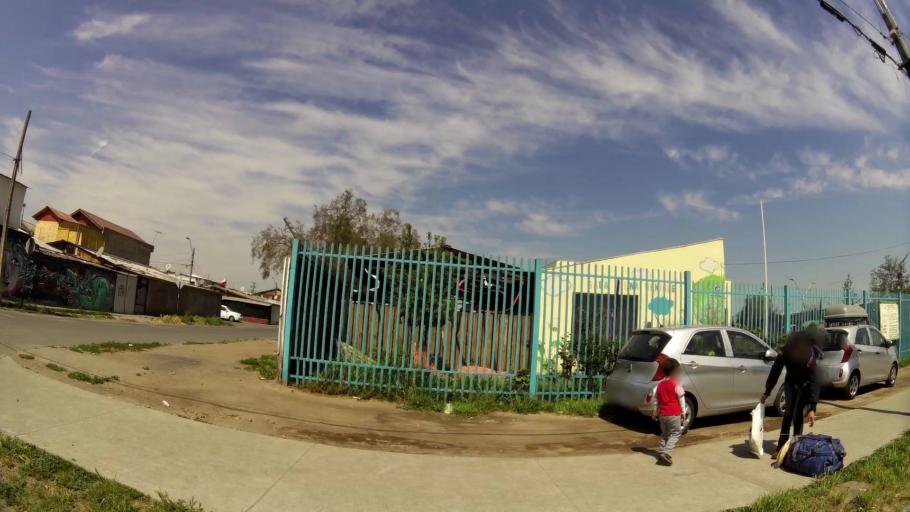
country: CL
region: Santiago Metropolitan
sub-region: Provincia de Santiago
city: La Pintana
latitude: -33.5502
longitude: -70.6404
